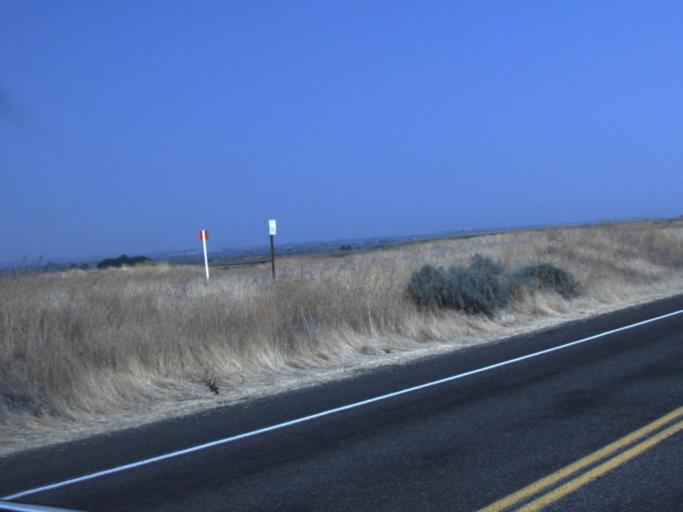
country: US
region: Washington
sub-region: Yakima County
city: Mabton
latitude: 46.2355
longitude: -120.0832
